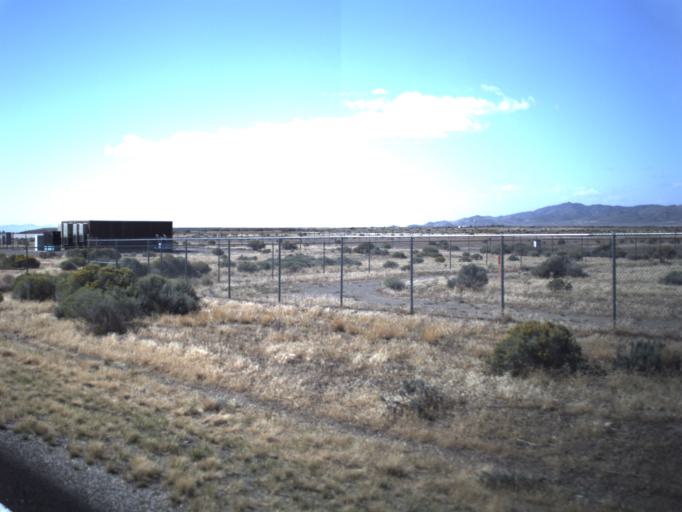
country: US
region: Utah
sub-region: Beaver County
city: Milford
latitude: 38.4221
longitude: -113.0099
